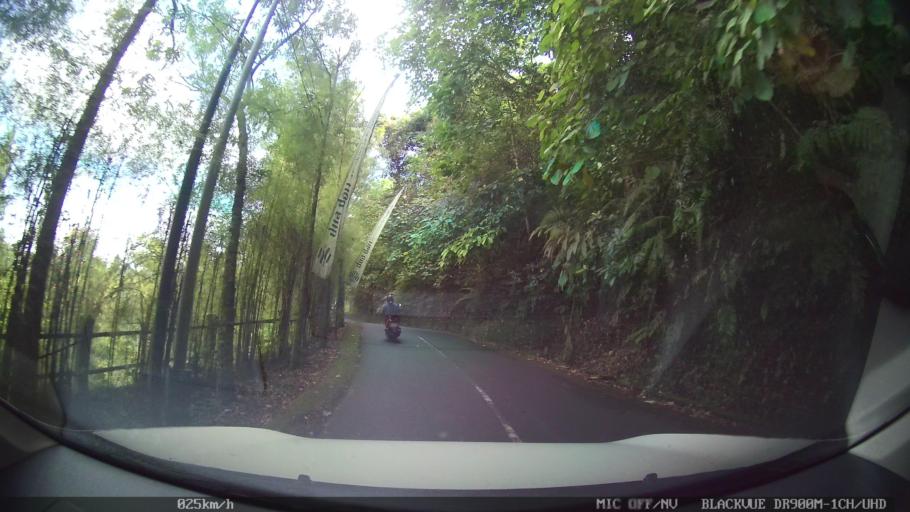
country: ID
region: Bali
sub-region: Kabupaten Gianyar
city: Ubud
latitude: -8.5086
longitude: 115.2783
